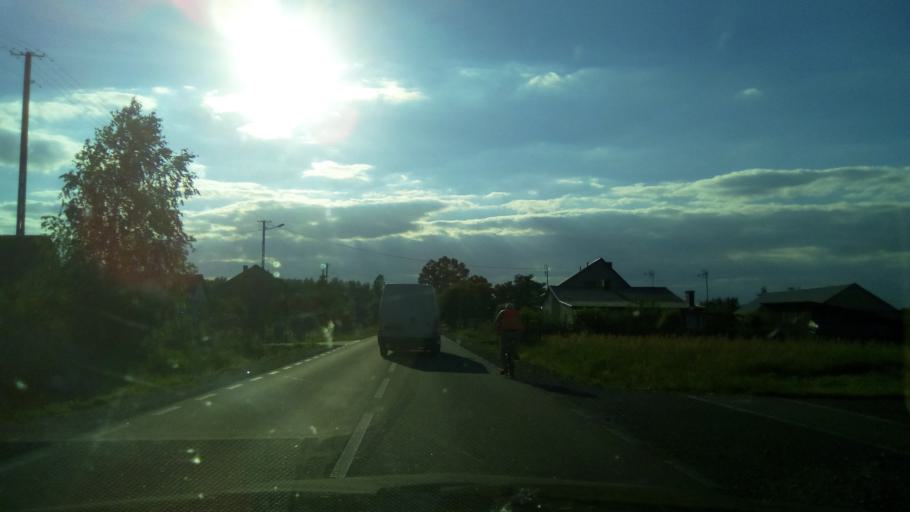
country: PL
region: Masovian Voivodeship
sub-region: Powiat bialobrzeski
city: Stromiec
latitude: 51.6445
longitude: 21.1435
